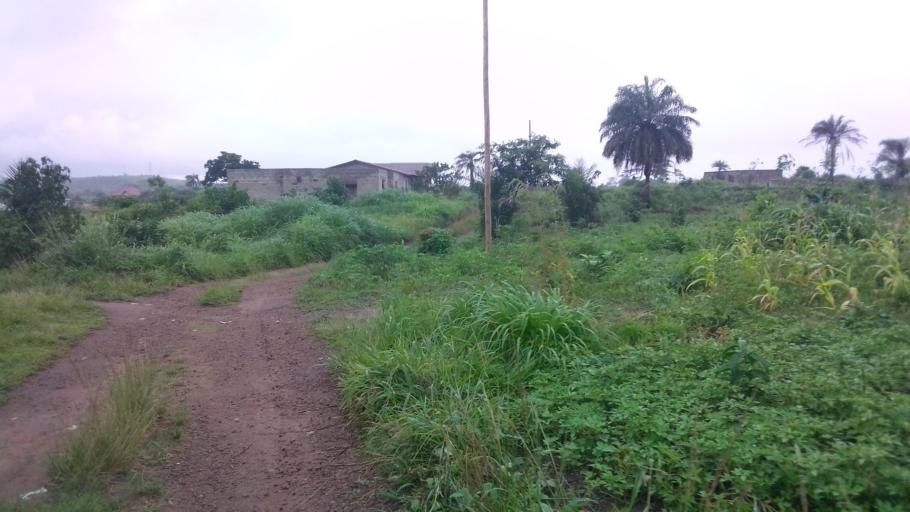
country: SL
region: Eastern Province
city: Kenema
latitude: 7.8306
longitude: -11.2084
